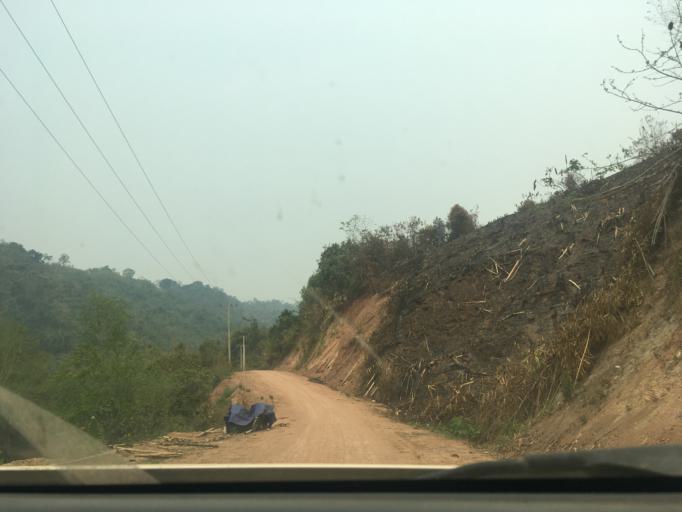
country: VN
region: Huyen Dien Bien
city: Thi Tran Muong Cha
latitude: 21.6531
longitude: 102.8258
